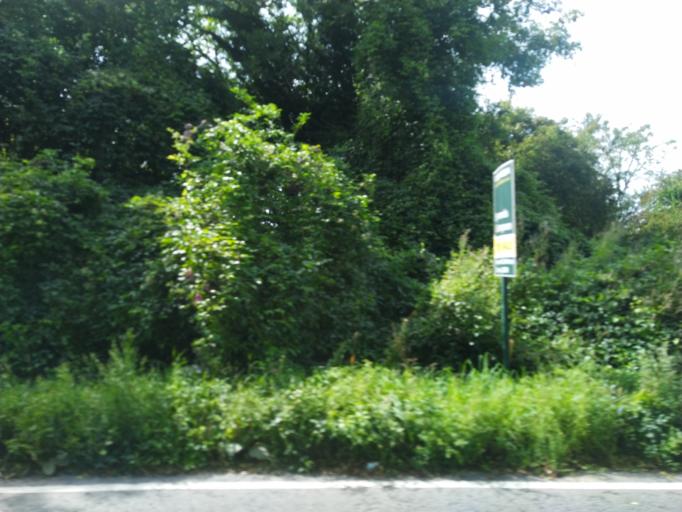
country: GB
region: England
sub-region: Dorset
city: Blandford Forum
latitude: 50.8781
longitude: -2.1952
